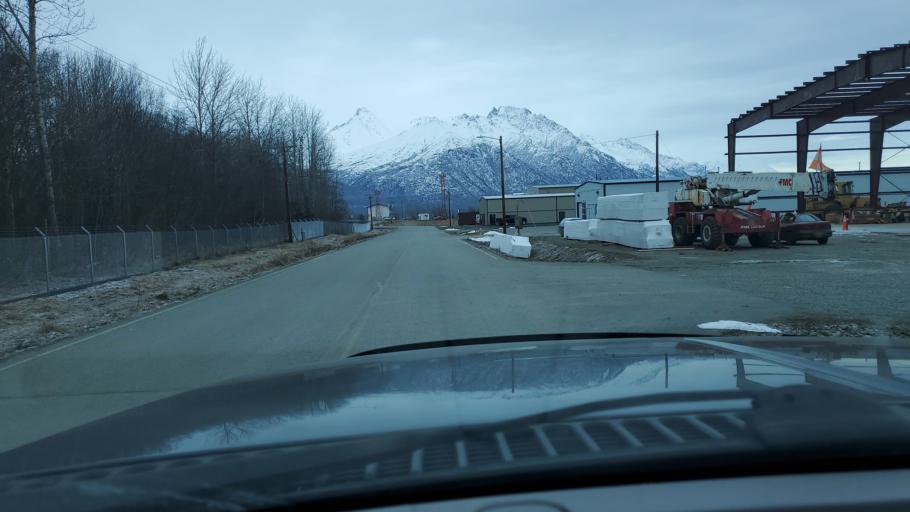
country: US
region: Alaska
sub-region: Matanuska-Susitna Borough
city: Palmer
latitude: 61.5964
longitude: -149.0985
